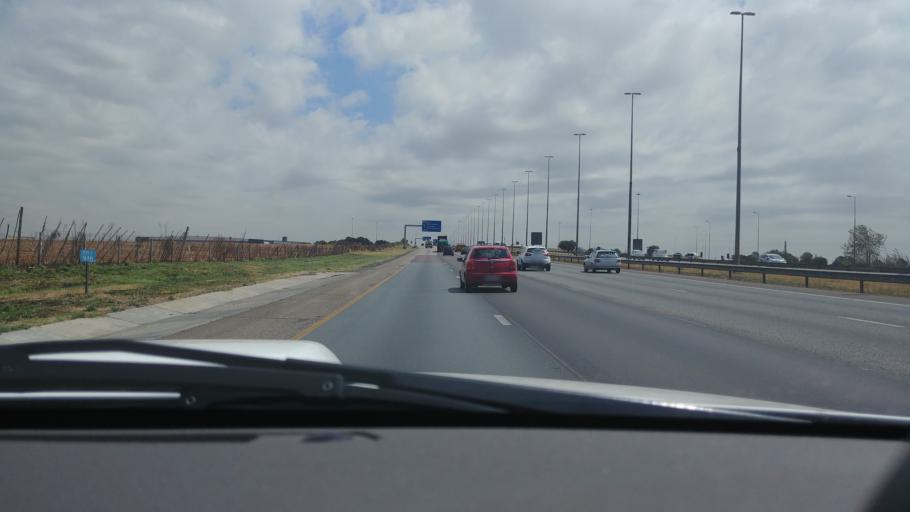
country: ZA
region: Gauteng
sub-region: Ekurhuleni Metropolitan Municipality
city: Tembisa
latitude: -26.0364
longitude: 28.2695
